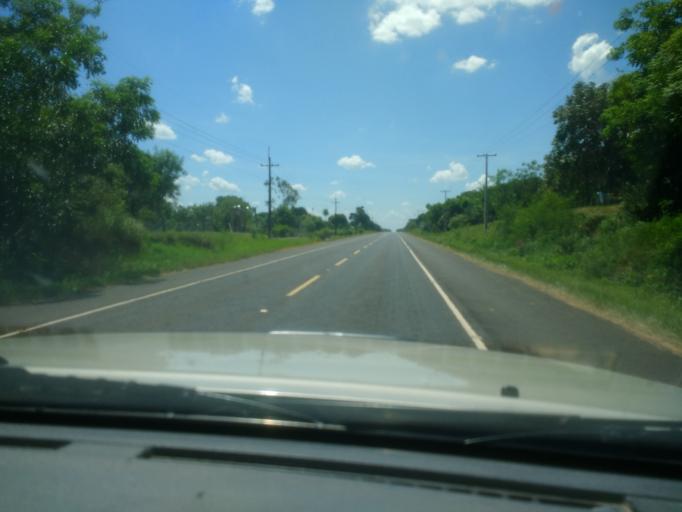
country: PY
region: San Pedro
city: General Elizardo Aquino
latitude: -24.4938
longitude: -56.8715
